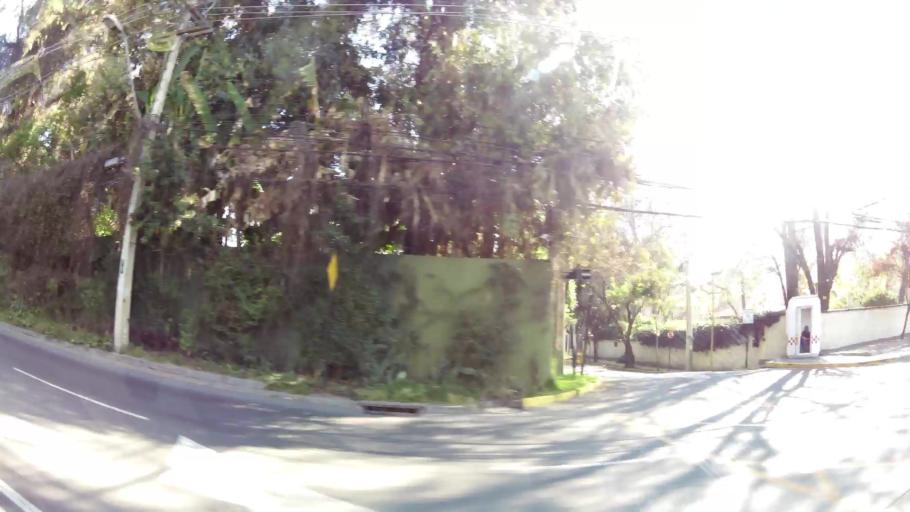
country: CL
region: Santiago Metropolitan
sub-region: Provincia de Santiago
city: Villa Presidente Frei, Nunoa, Santiago, Chile
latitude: -33.3748
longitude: -70.5164
